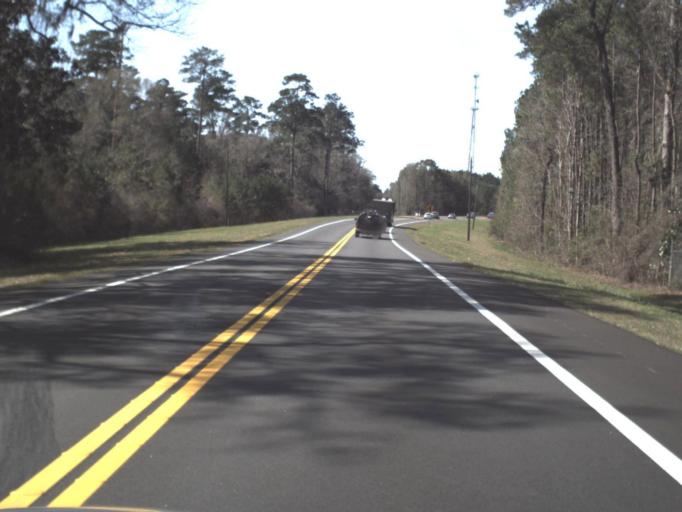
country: US
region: Florida
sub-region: Gadsden County
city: Quincy
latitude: 30.3874
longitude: -84.6431
